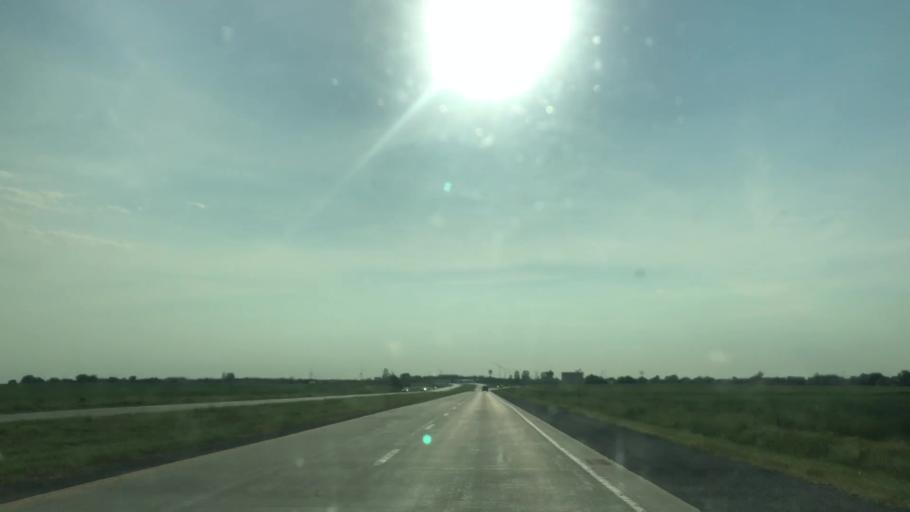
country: US
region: Iowa
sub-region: Story County
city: Nevada
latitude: 42.0081
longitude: -93.4216
